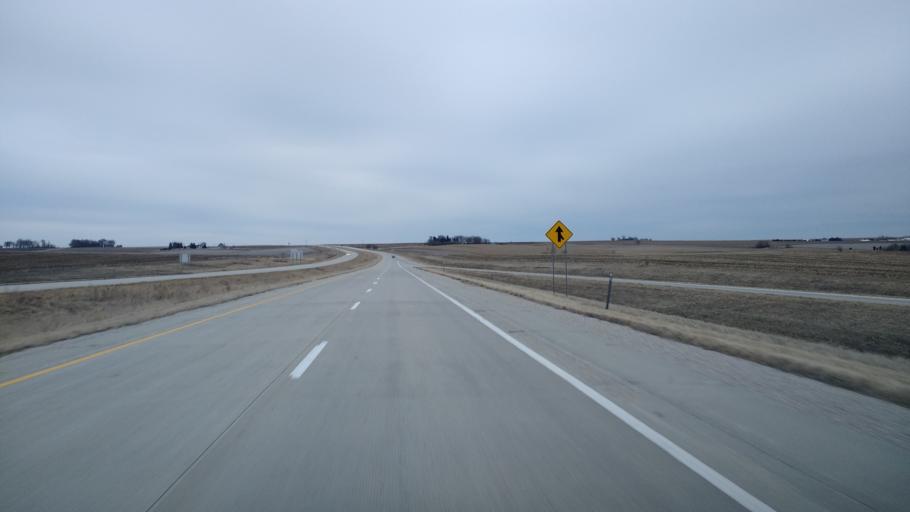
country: US
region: Iowa
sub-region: Sac County
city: Sac City
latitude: 42.4714
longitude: -95.1450
